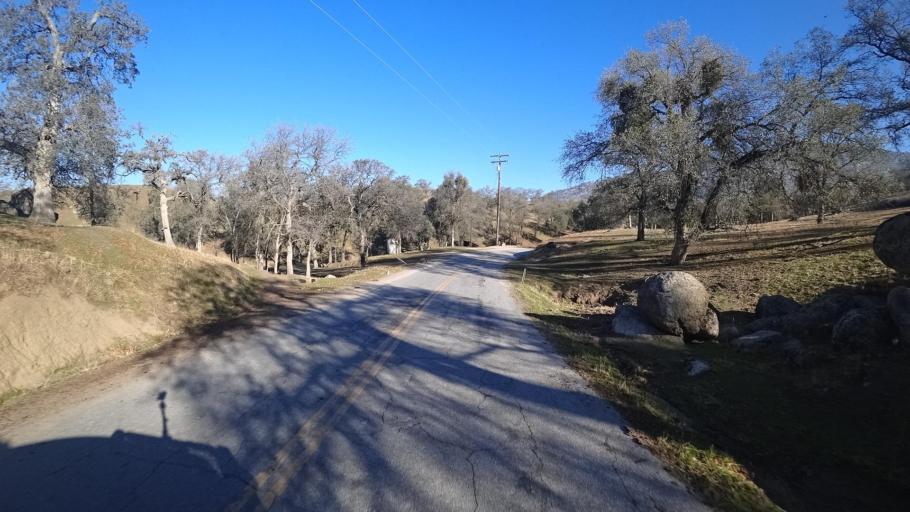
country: US
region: California
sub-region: Kern County
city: Alta Sierra
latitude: 35.7432
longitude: -118.8186
